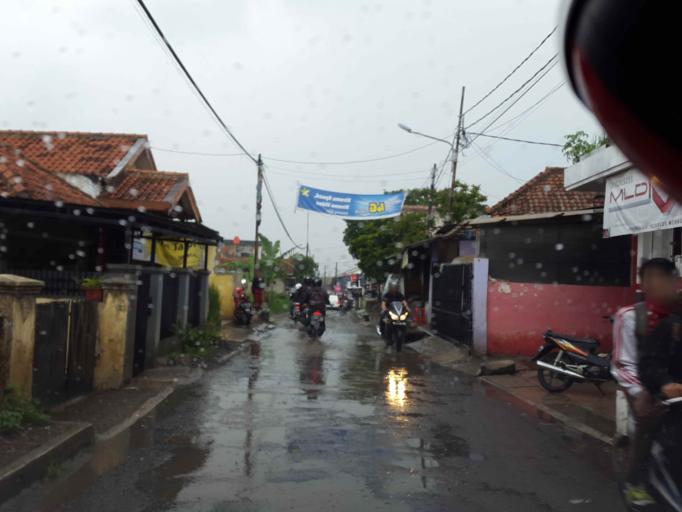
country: ID
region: West Java
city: Cimahi
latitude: -6.8729
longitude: 107.5613
